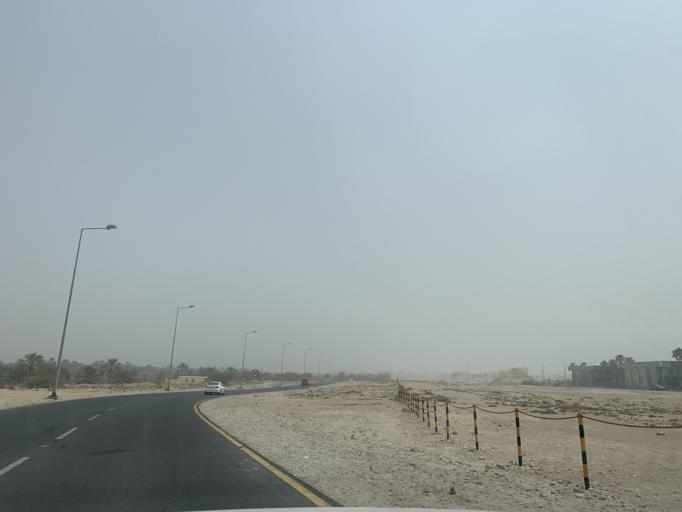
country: BH
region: Central Governorate
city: Madinat Hamad
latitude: 26.1738
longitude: 50.4836
